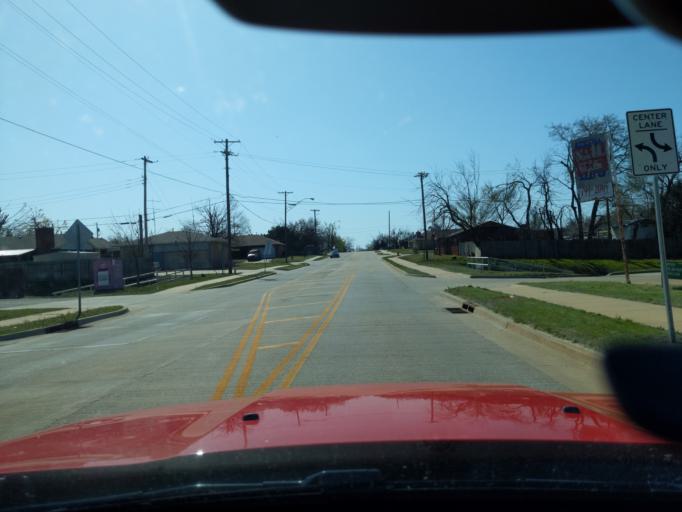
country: US
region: Oklahoma
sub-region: Cleveland County
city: Moore
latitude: 35.3482
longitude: -97.4903
